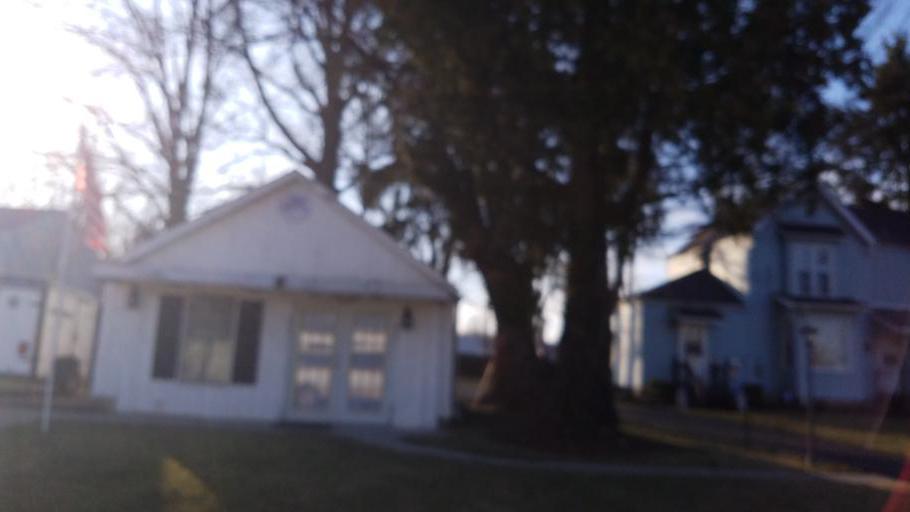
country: US
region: Ohio
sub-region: Richland County
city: Ontario
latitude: 40.7600
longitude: -82.6475
